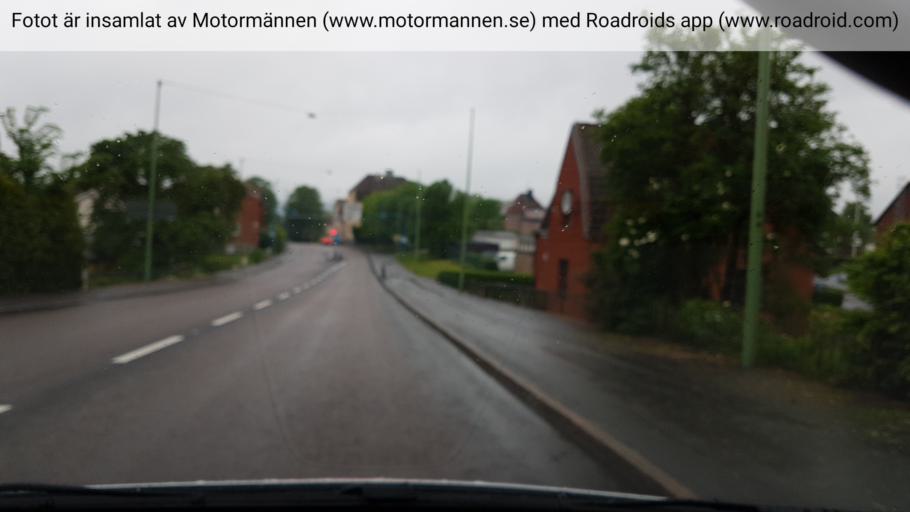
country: SE
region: Vaestra Goetaland
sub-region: Falkopings Kommun
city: Falkoeping
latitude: 58.1641
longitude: 13.5595
